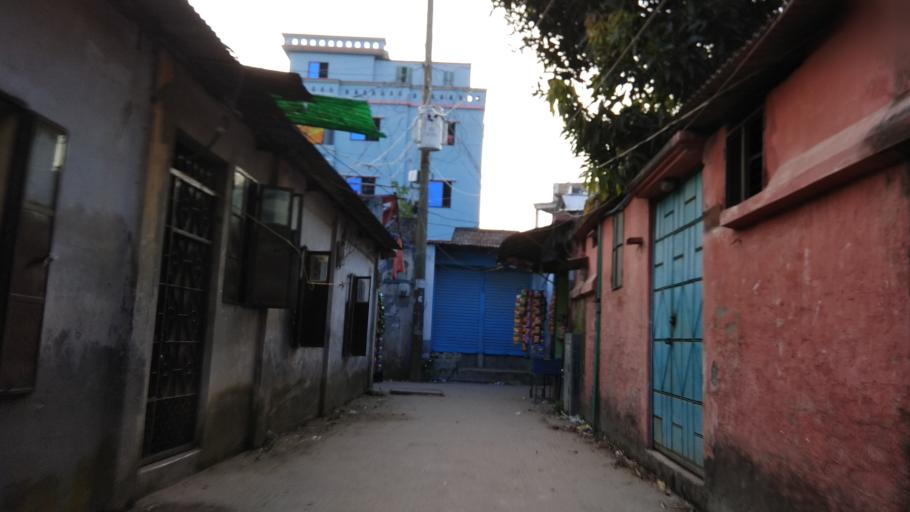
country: BD
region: Dhaka
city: Azimpur
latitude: 23.8001
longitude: 90.3402
